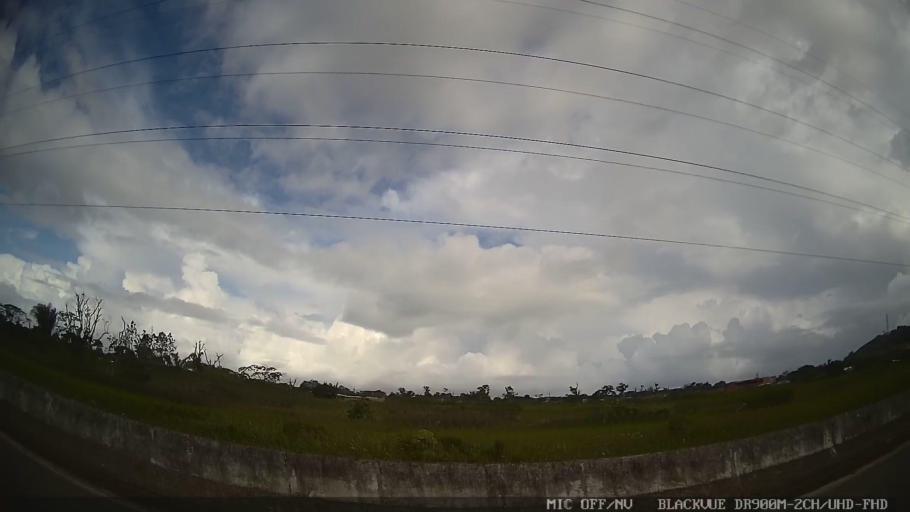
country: BR
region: Sao Paulo
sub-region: Peruibe
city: Peruibe
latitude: -24.2606
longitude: -46.9456
